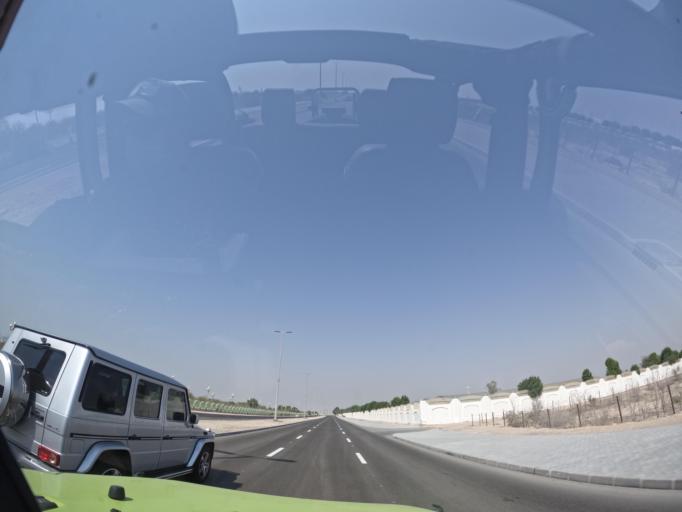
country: AE
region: Abu Dhabi
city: Abu Dhabi
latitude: 24.4690
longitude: 54.6280
